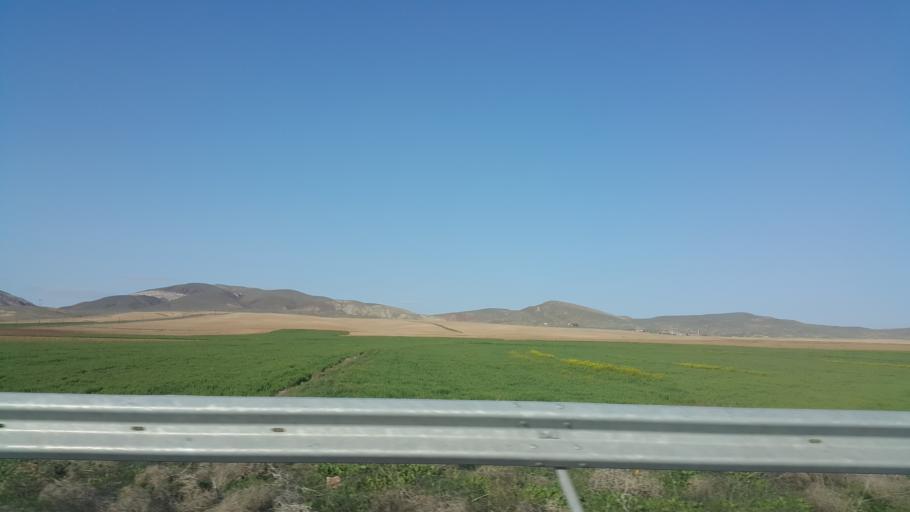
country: TR
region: Aksaray
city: Acipinar
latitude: 38.6897
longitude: 33.6930
